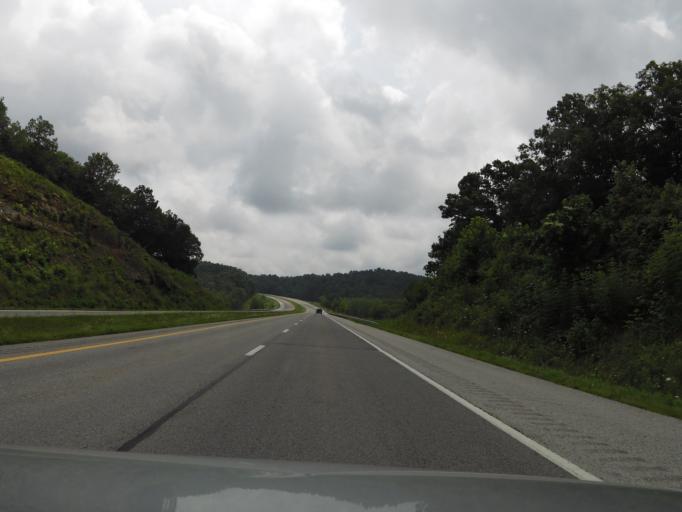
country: US
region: Kentucky
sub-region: Ohio County
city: Oak Grove
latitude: 37.3891
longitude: -86.7009
